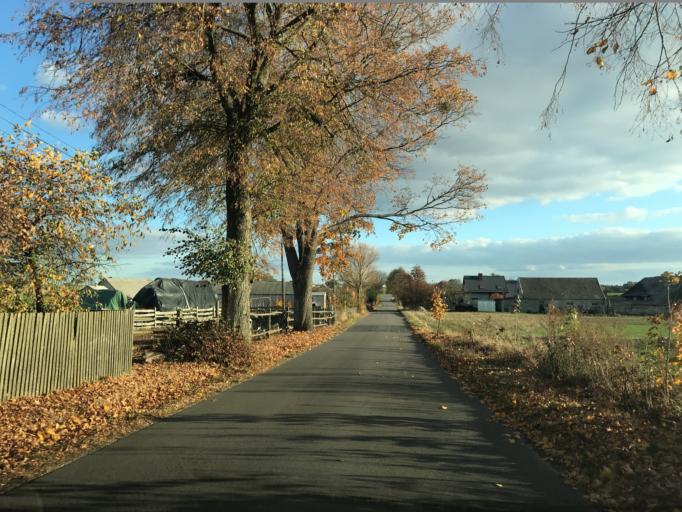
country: PL
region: Warmian-Masurian Voivodeship
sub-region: Powiat dzialdowski
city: Lidzbark
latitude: 53.3569
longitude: 19.8047
